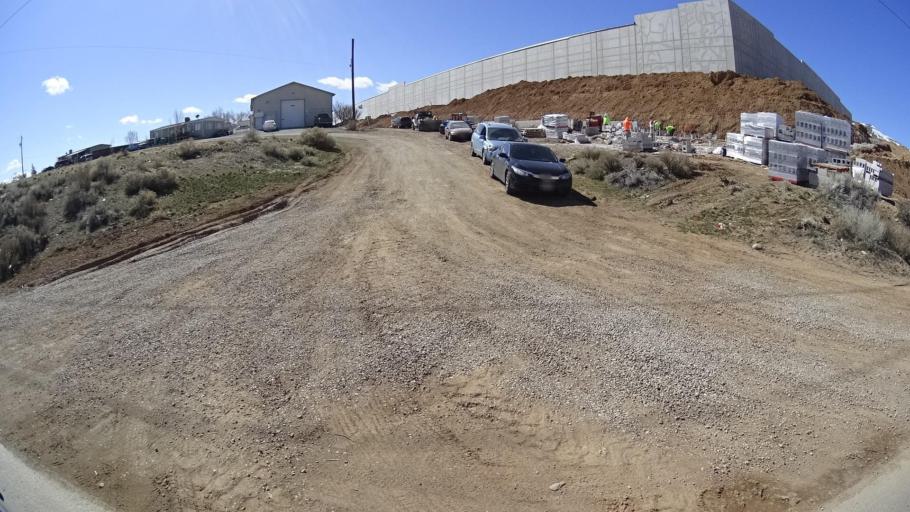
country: US
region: Nevada
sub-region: Washoe County
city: Lemmon Valley
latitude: 39.6063
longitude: -119.8594
